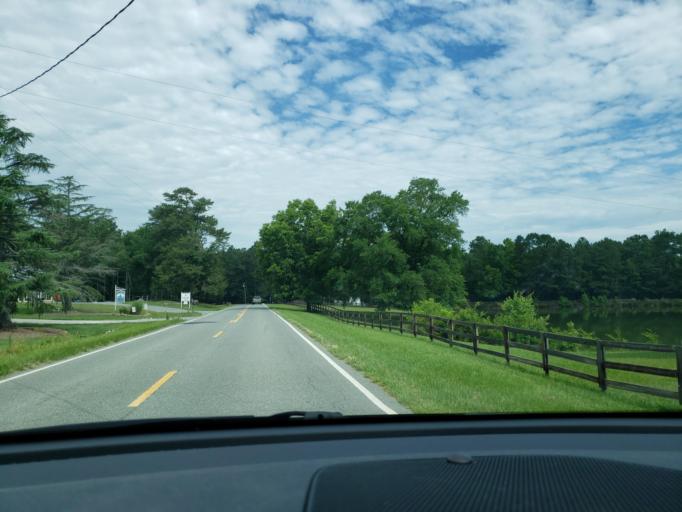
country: US
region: North Carolina
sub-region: Wake County
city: Green Level
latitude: 35.7935
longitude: -78.9734
